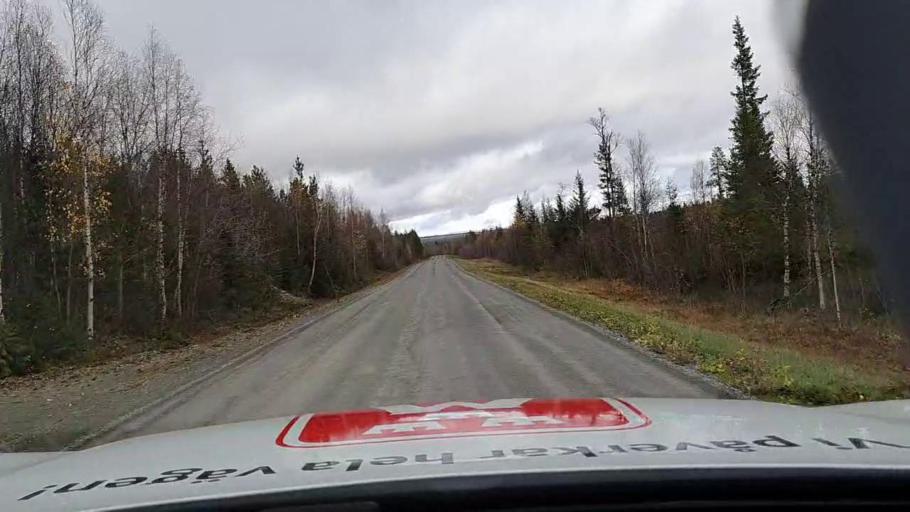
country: SE
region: Jaemtland
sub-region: Krokoms Kommun
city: Valla
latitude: 63.0527
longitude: 13.9635
